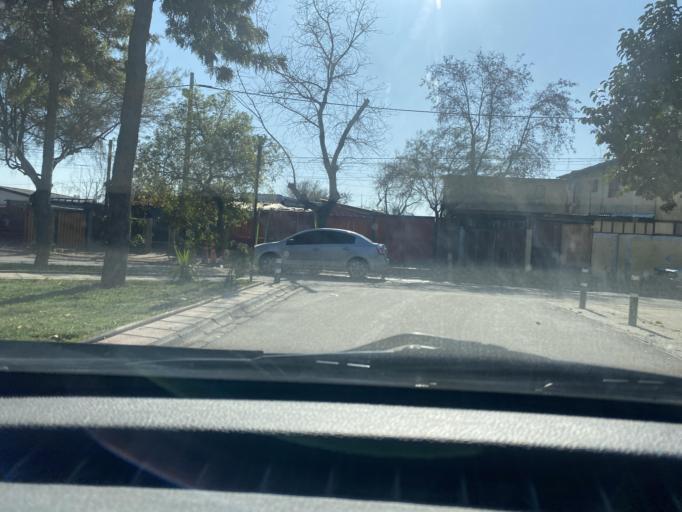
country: CL
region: Santiago Metropolitan
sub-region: Provincia de Santiago
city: La Pintana
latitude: -33.5398
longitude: -70.6144
